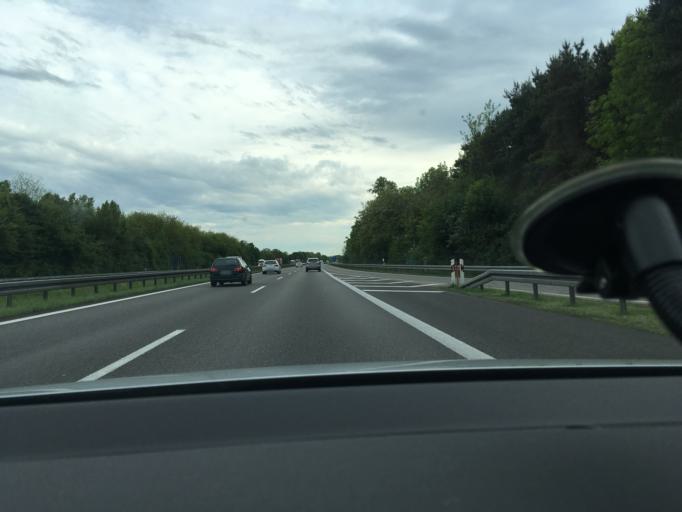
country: DE
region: Baden-Wuerttemberg
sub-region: Freiburg Region
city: Neuenburg am Rhein
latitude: 47.8288
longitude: 7.5623
